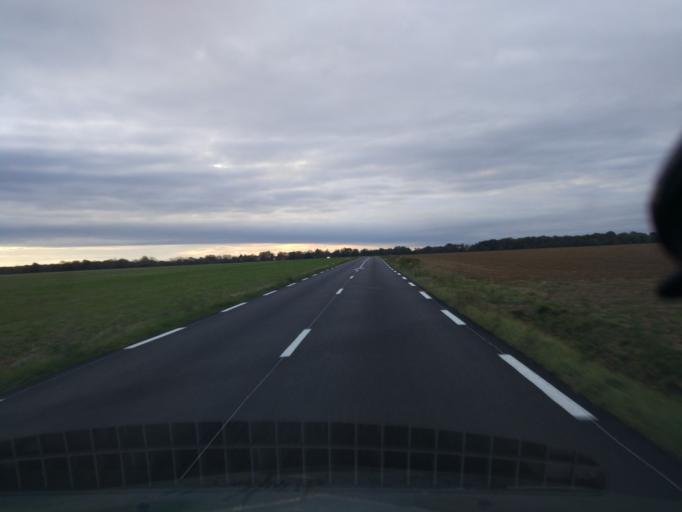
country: FR
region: Ile-de-France
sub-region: Departement de l'Essonne
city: Les Molieres
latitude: 48.6599
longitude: 2.0660
